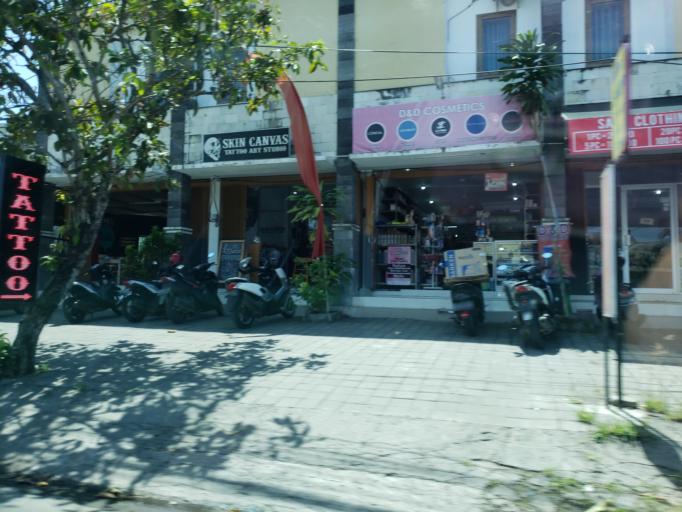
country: ID
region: Bali
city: Kangin
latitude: -8.8296
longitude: 115.1360
